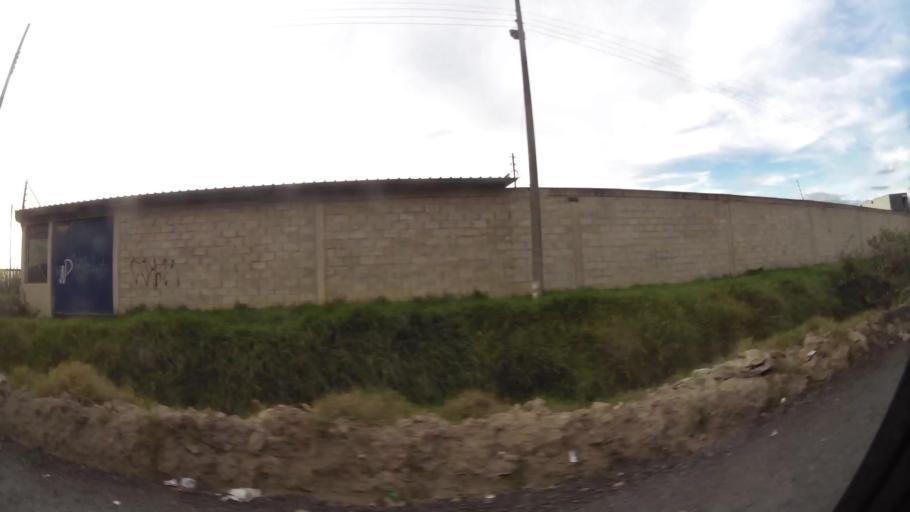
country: CO
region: Cundinamarca
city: Funza
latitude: 4.6951
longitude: -74.1754
